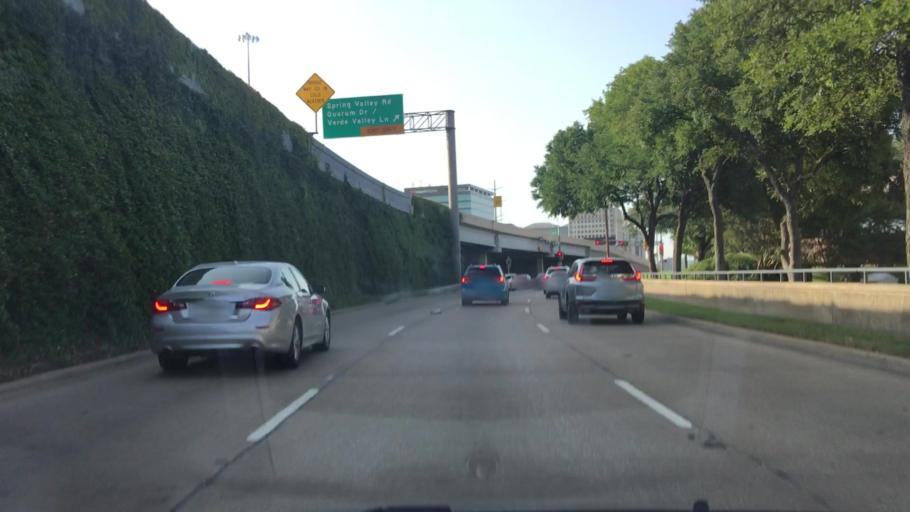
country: US
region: Texas
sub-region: Dallas County
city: Addison
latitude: 32.9319
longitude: -96.8216
